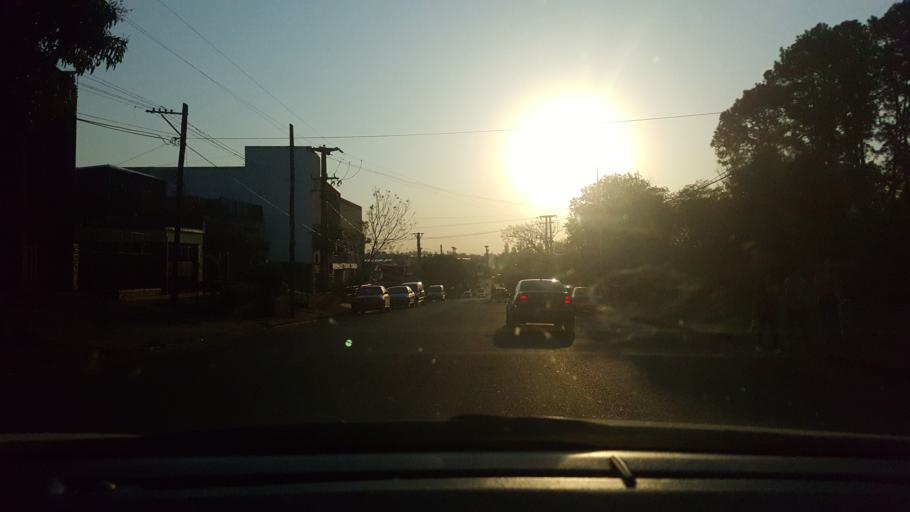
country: AR
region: Misiones
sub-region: Departamento de Capital
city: Posadas
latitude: -27.4050
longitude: -55.8976
